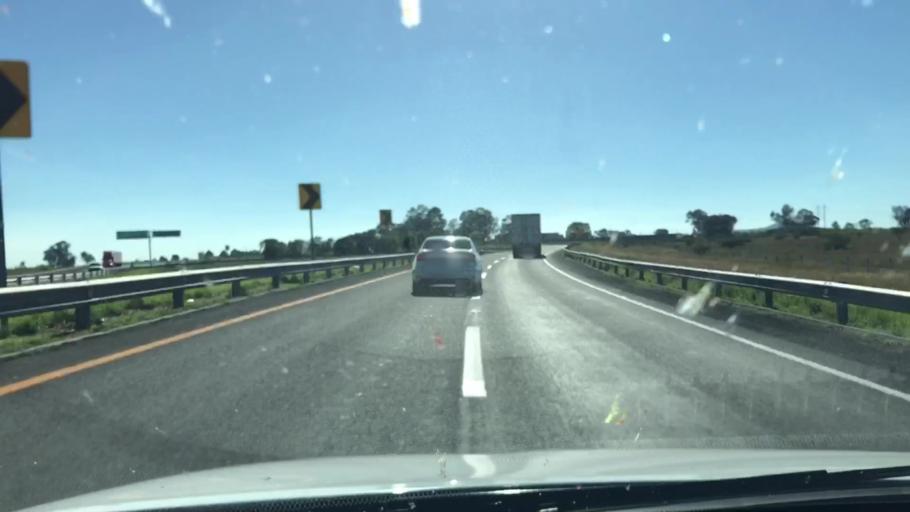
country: MX
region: Jalisco
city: Tepatitlan de Morelos
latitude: 20.9030
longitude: -102.6963
